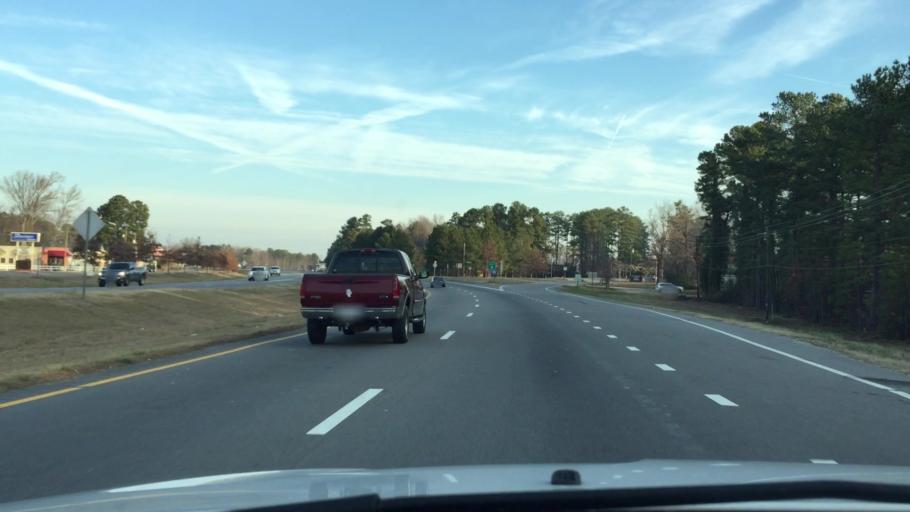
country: US
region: North Carolina
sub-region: Lee County
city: Sanford
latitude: 35.4428
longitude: -79.2153
